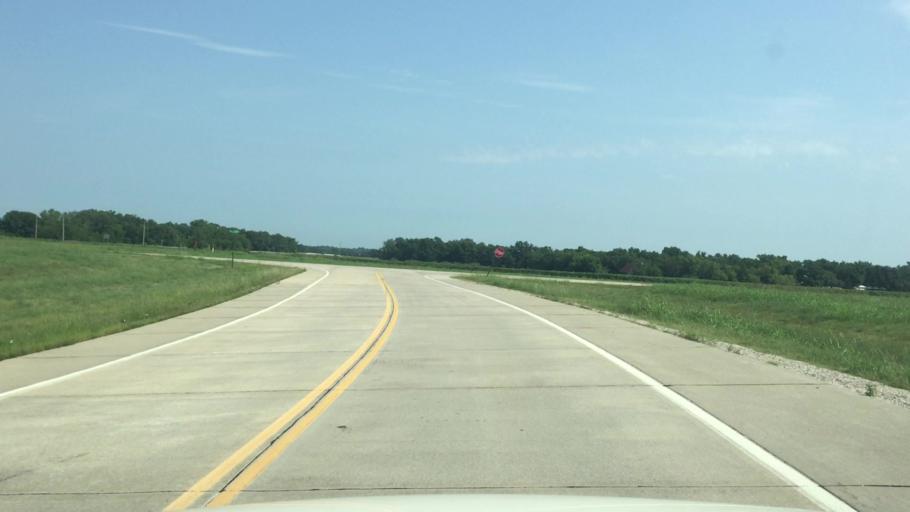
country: US
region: Kansas
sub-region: Montgomery County
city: Coffeyville
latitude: 37.1069
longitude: -95.5842
